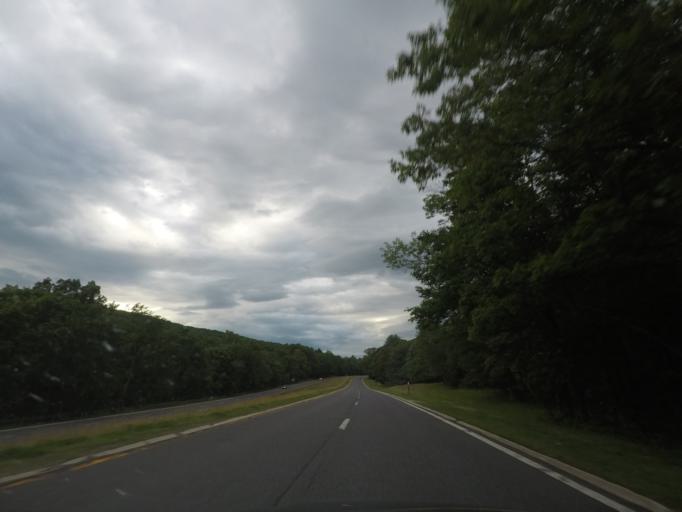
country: US
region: New York
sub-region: Dutchess County
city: Pine Plains
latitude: 42.0327
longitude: -73.7327
